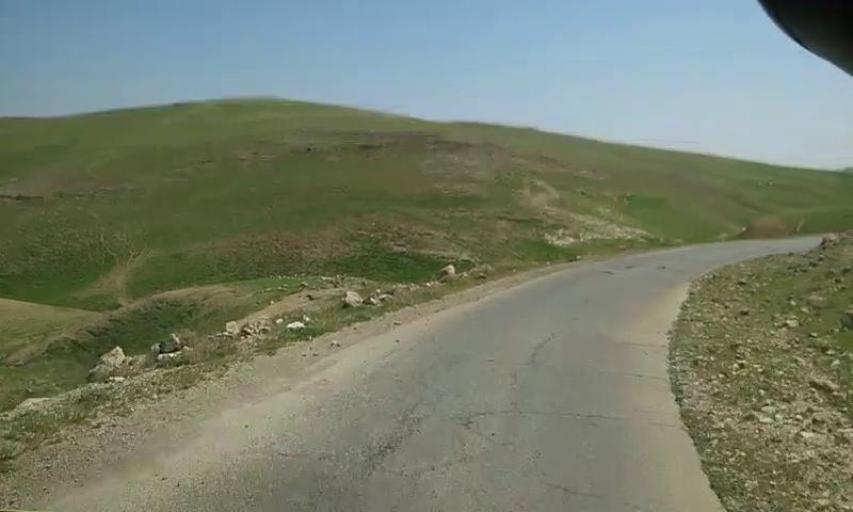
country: PS
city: `Arab ar Rashaydah
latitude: 31.5556
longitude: 35.2488
